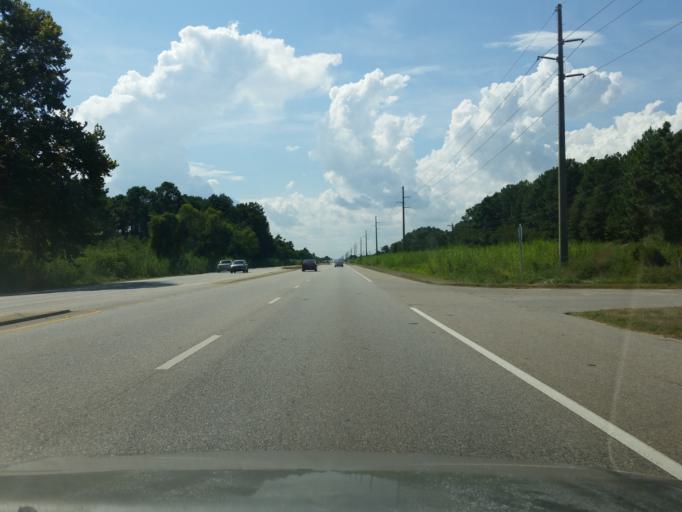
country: US
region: Alabama
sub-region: Baldwin County
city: Spanish Fort
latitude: 30.6691
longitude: -87.9311
